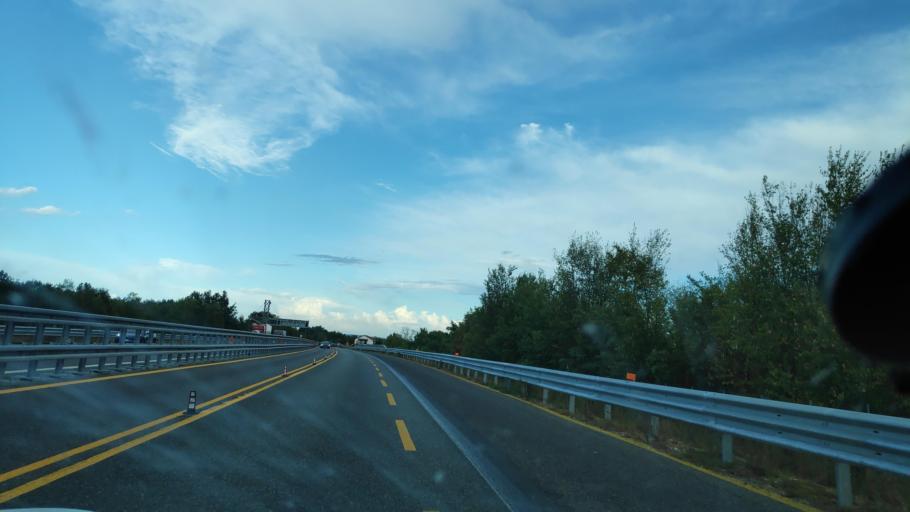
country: IT
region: Piedmont
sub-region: Provincia di Asti
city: Castello di Annone
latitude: 44.9093
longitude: 8.3199
